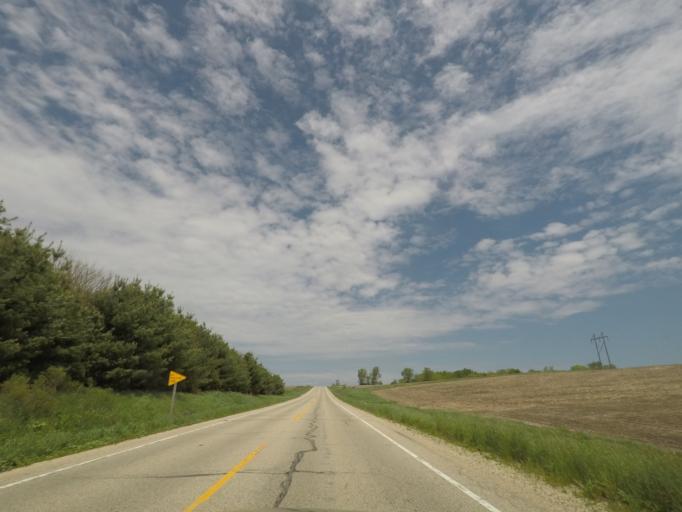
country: US
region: Wisconsin
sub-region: Rock County
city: Orfordville
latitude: 42.6645
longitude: -89.2883
